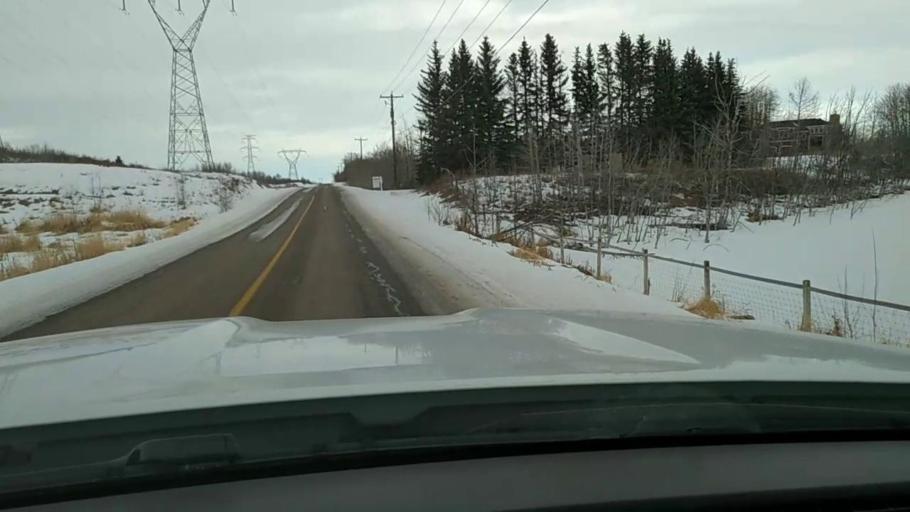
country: CA
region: Alberta
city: Cochrane
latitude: 51.1766
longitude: -114.2575
